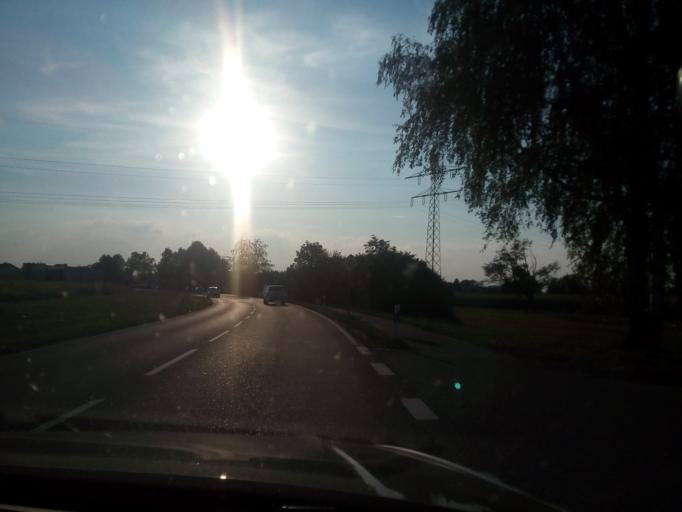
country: DE
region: Baden-Wuerttemberg
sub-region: Karlsruhe Region
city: Ottenhofen
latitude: 48.7286
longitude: 8.0944
